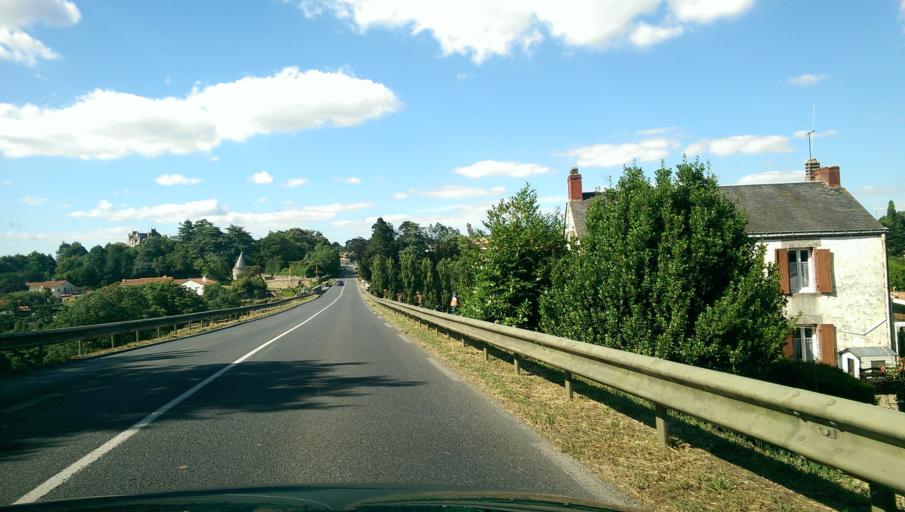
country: FR
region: Pays de la Loire
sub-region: Departement de la Vendee
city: Rocheserviere
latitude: 46.9342
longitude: -1.5148
